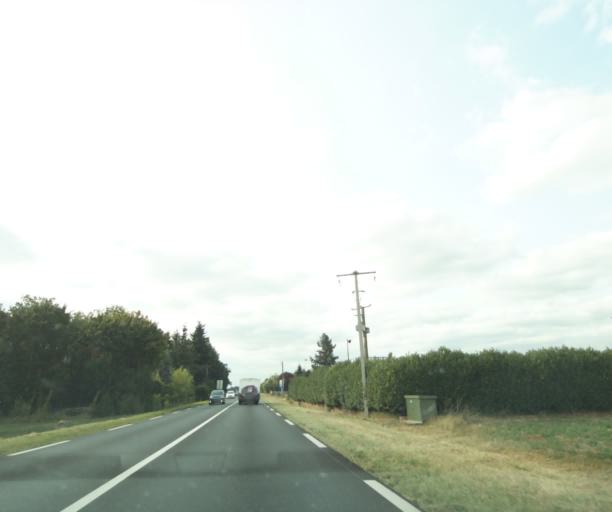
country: FR
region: Centre
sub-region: Departement d'Indre-et-Loire
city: Esvres
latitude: 47.2927
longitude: 0.8078
